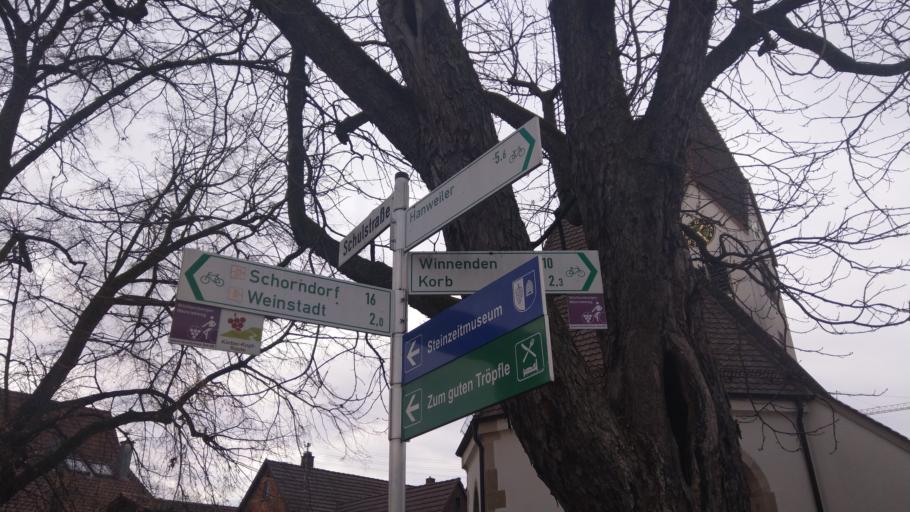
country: DE
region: Baden-Wuerttemberg
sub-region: Regierungsbezirk Stuttgart
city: Korb
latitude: 48.8292
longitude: 9.3748
